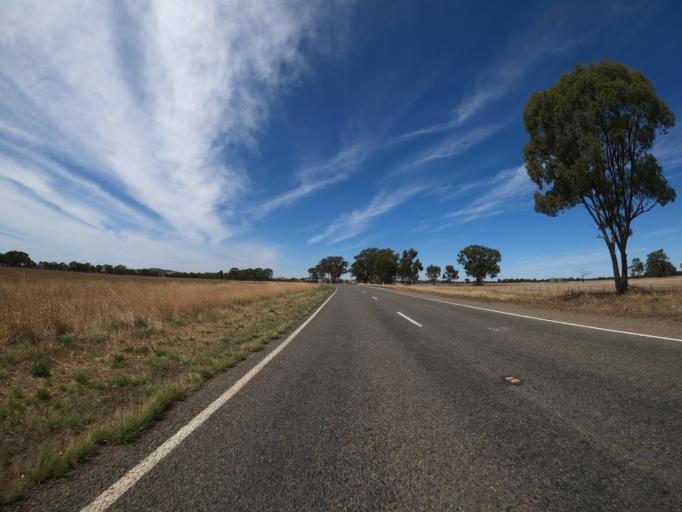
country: AU
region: Victoria
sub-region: Benalla
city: Benalla
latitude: -36.2974
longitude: 145.9523
